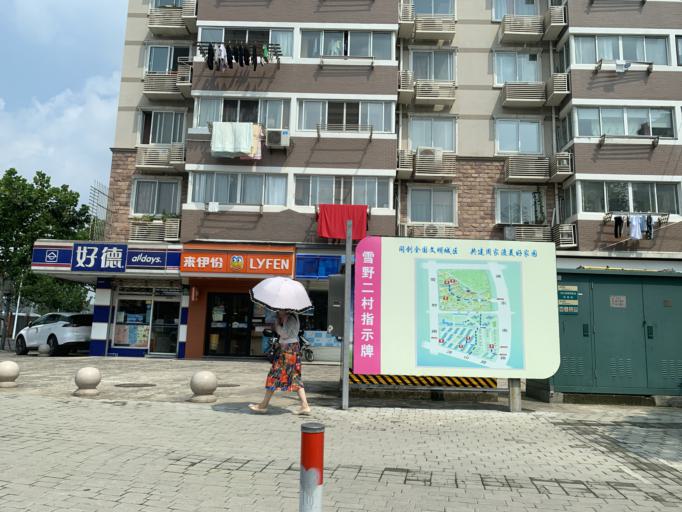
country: CN
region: Shanghai Shi
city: Luwan
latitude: 31.1820
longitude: 121.4936
